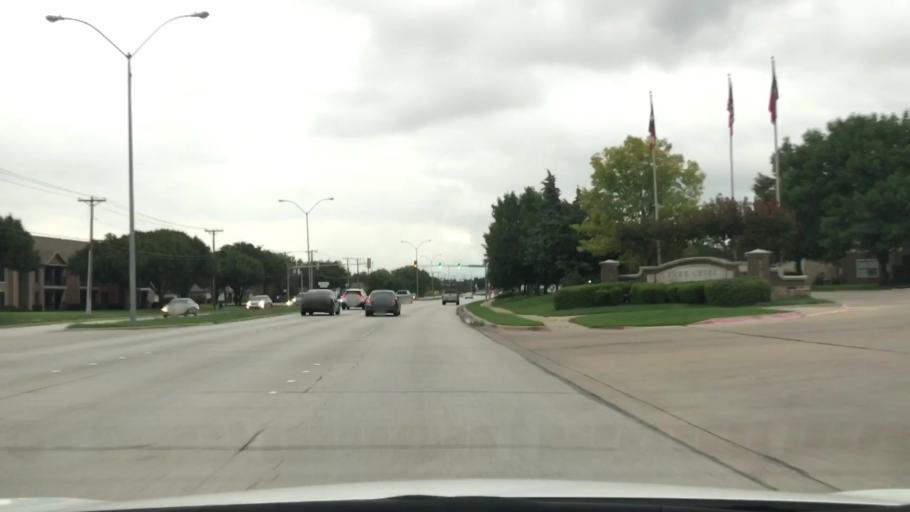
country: US
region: Texas
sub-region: Tarrant County
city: Watauga
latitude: 32.8655
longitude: -97.2912
